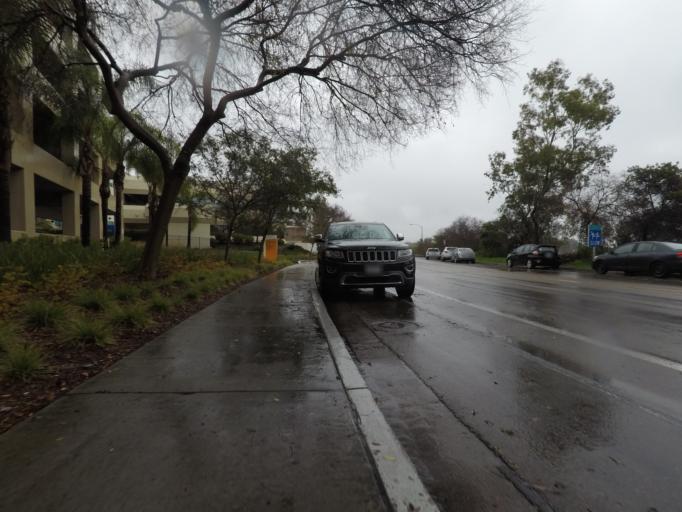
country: US
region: California
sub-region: San Diego County
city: San Diego
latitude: 32.7968
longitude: -117.1528
